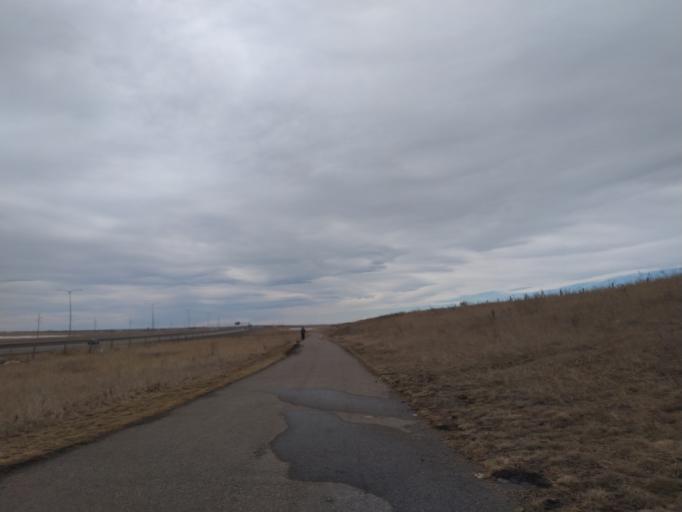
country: CA
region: Alberta
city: Chestermere
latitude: 51.1180
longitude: -113.9224
